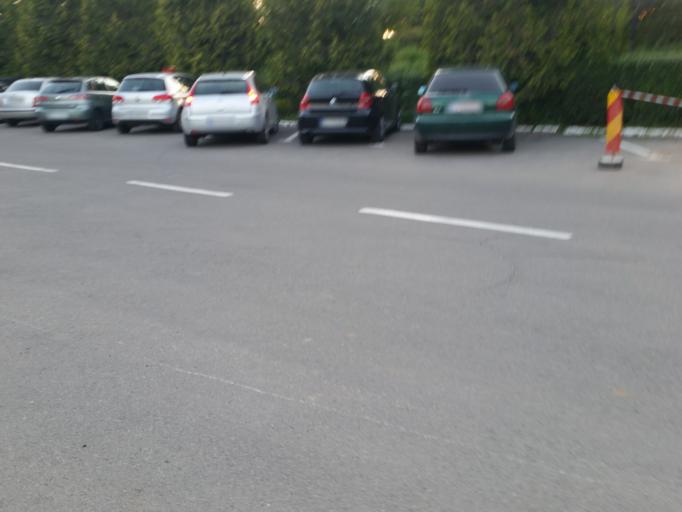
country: RO
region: Cluj
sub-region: Municipiul Cluj-Napoca
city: Cluj-Napoca
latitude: 46.7752
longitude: 23.5820
